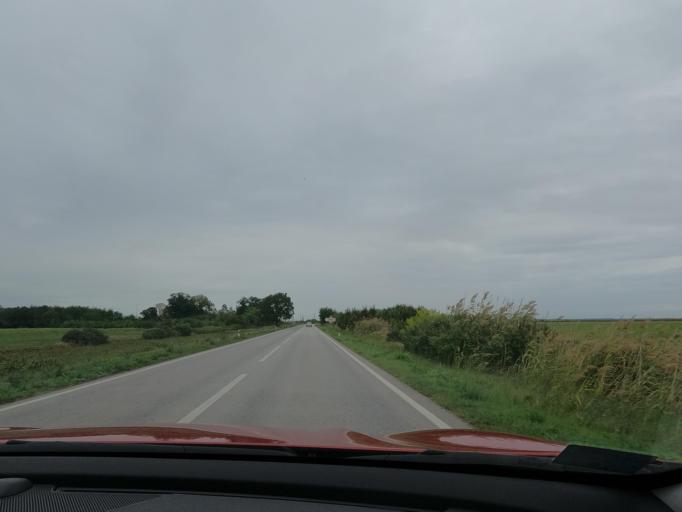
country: RS
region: Autonomna Pokrajina Vojvodina
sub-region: Severnobanatski Okrug
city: Kikinda
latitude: 45.7651
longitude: 20.4231
